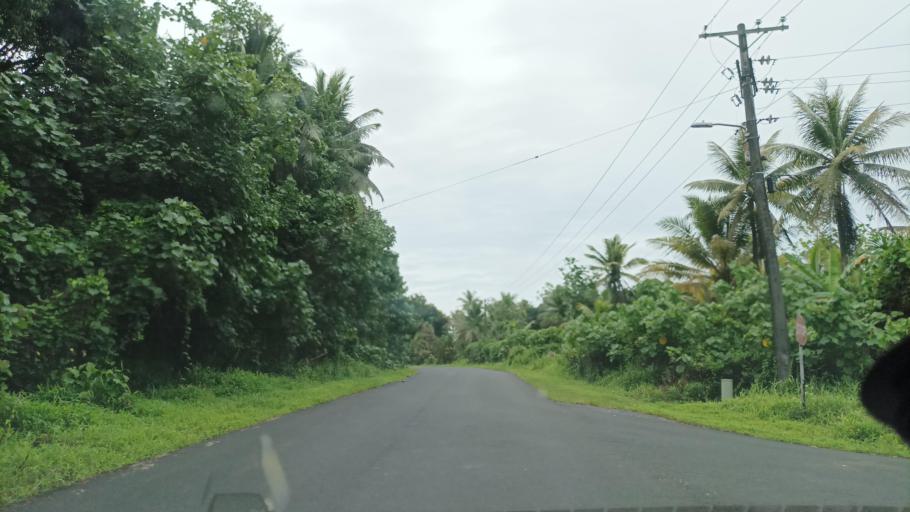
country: FM
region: Pohnpei
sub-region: Madolenihm Municipality
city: Madolenihm Municipality Government
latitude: 6.8981
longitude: 158.3159
